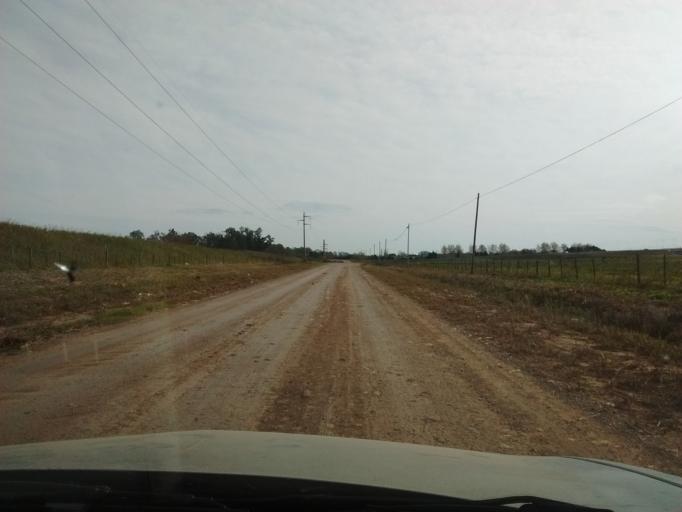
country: AR
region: Santa Fe
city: Funes
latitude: -32.9425
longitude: -60.8139
